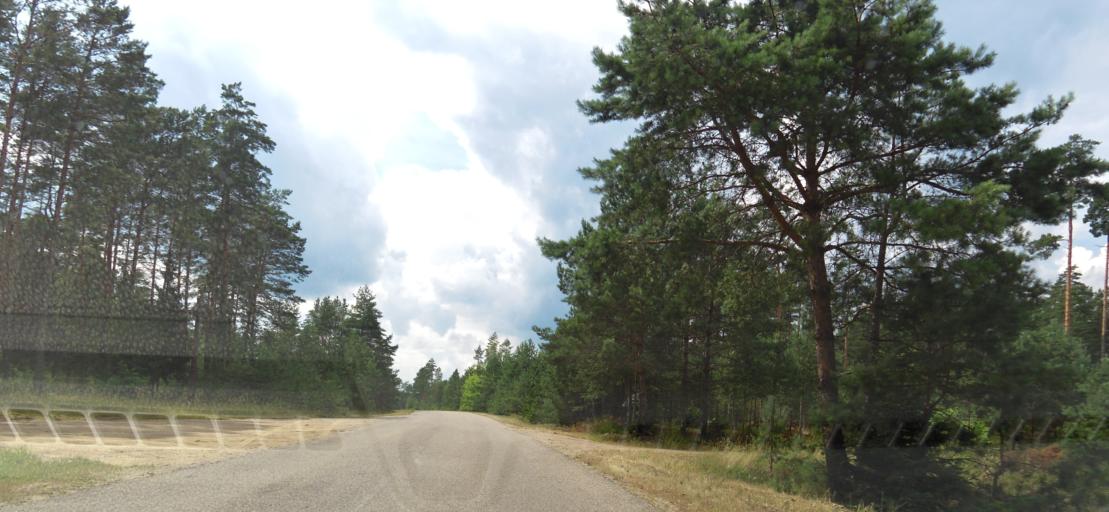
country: LT
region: Alytaus apskritis
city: Druskininkai
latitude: 53.9882
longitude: 24.0923
